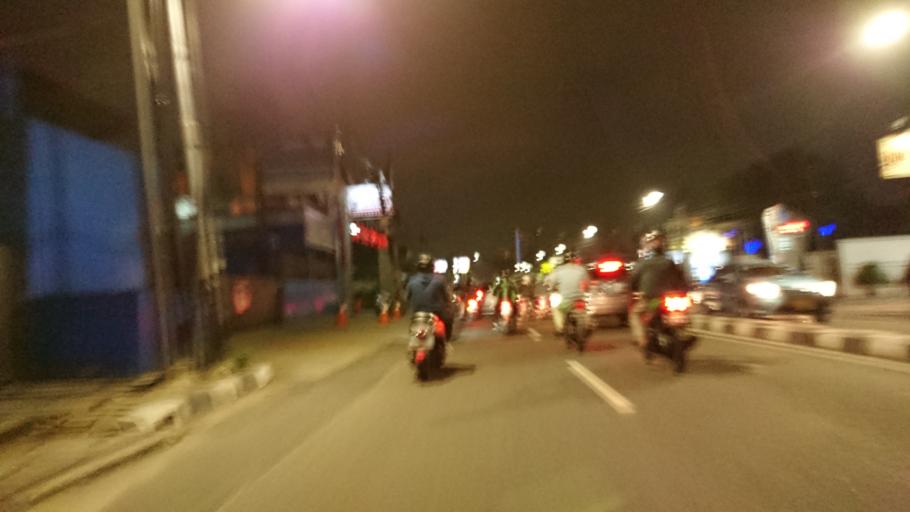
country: ID
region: Jakarta Raya
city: Jakarta
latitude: -6.1997
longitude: 106.8013
